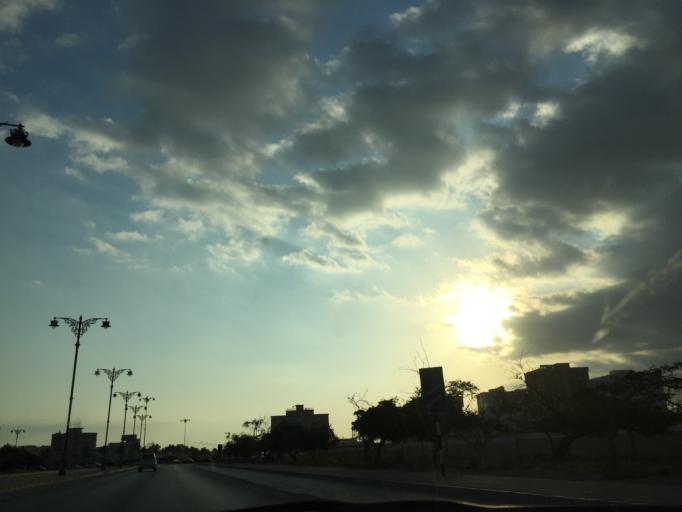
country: OM
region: Zufar
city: Salalah
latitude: 17.0074
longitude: 54.0421
